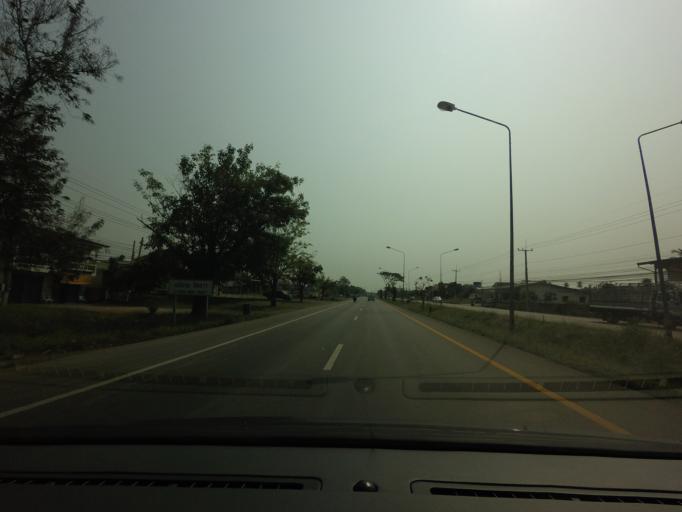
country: TH
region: Prachuap Khiri Khan
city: Sam Roi Yot
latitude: 12.2362
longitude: 99.8698
